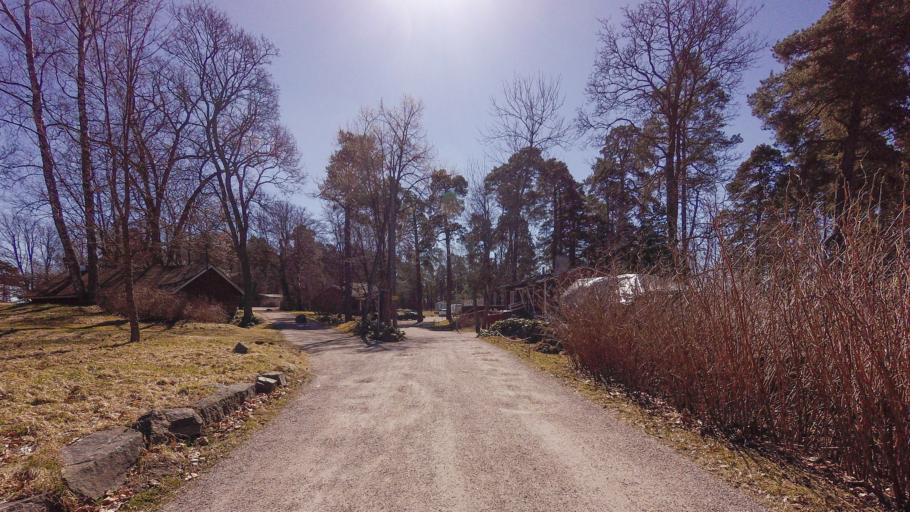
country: FI
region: Uusimaa
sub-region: Helsinki
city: Helsinki
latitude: 60.1637
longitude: 25.0289
